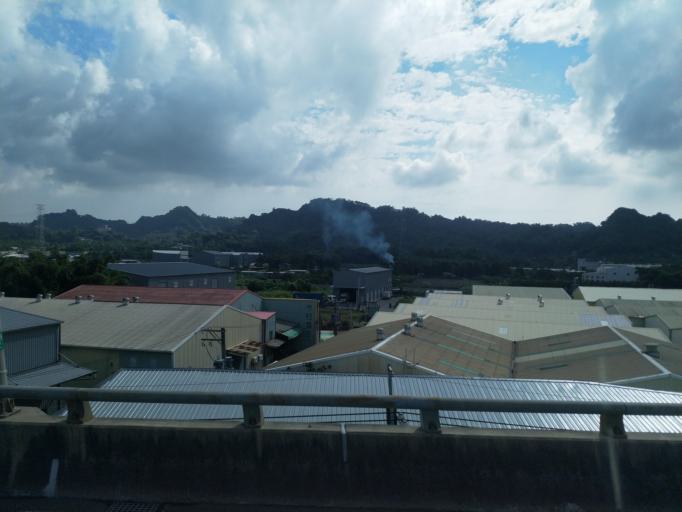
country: TW
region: Taiwan
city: Fengshan
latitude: 22.7275
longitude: 120.3605
